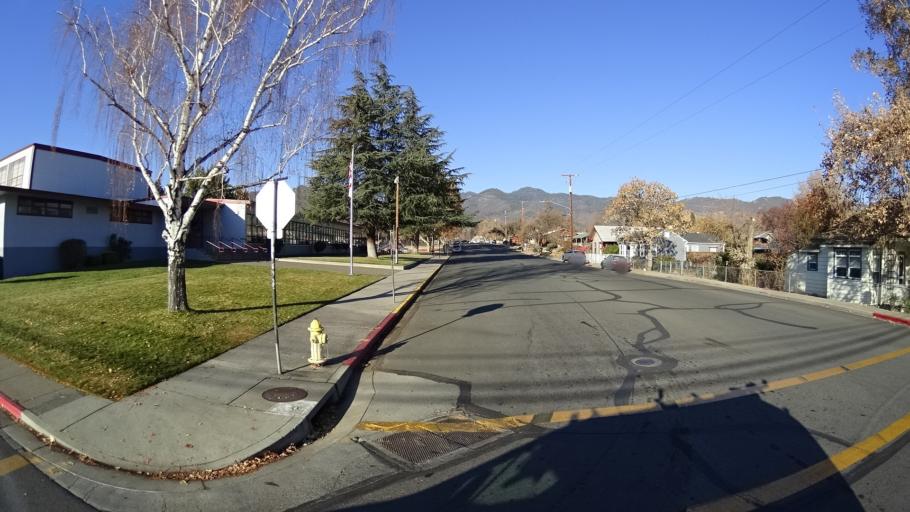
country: US
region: California
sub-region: Siskiyou County
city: Yreka
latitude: 41.7281
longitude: -122.6400
